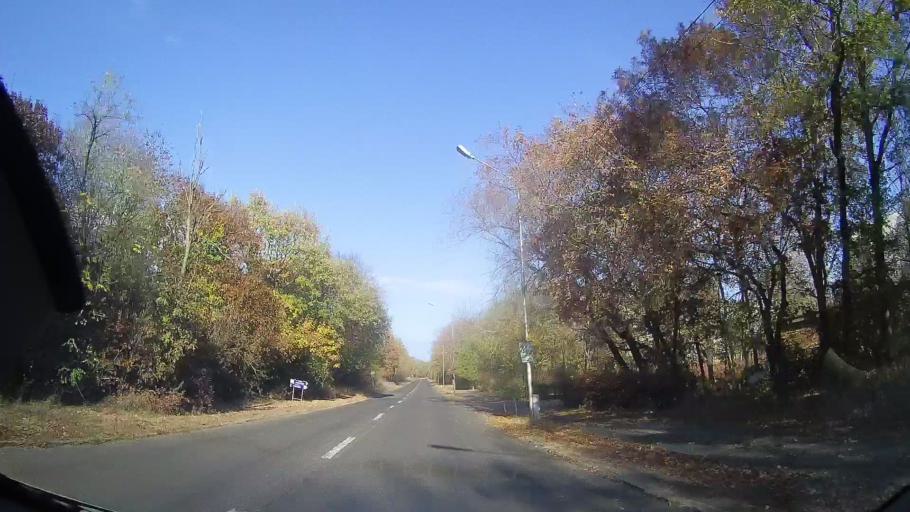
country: RO
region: Constanta
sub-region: Comuna Douazeci si Trei August
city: Douazeci si Trei August
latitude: 43.8708
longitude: 28.5950
